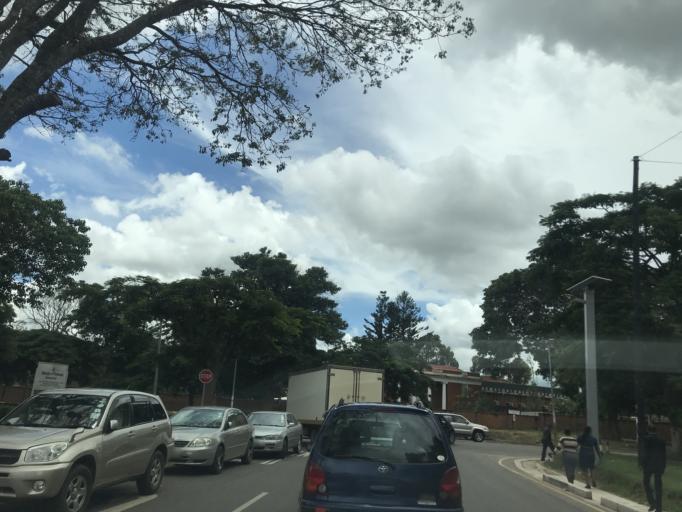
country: ZM
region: Lusaka
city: Lusaka
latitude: -15.4210
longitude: 28.3063
